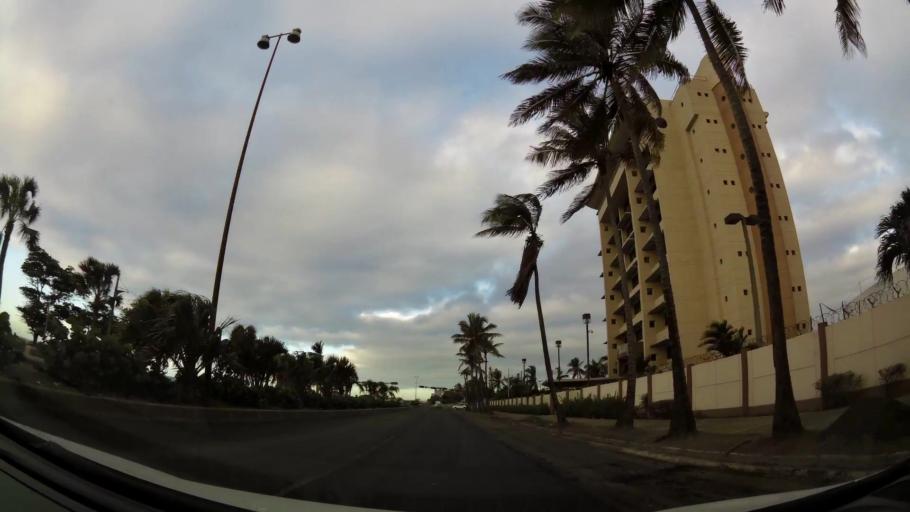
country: DO
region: Nacional
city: Bella Vista
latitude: 18.4374
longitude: -69.9388
